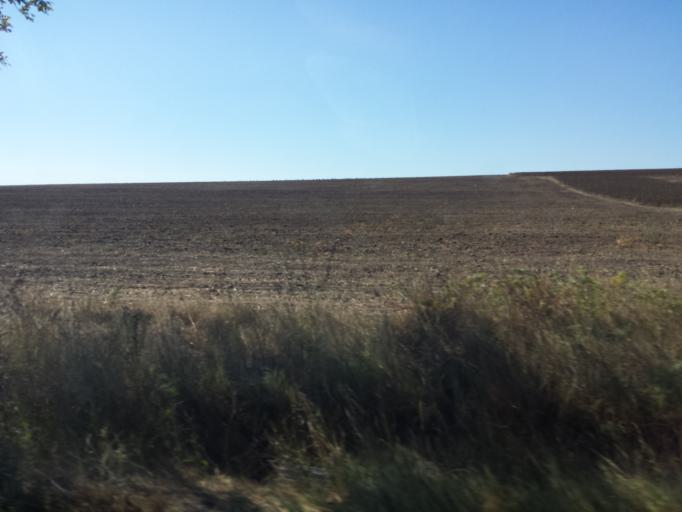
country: RO
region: Tulcea
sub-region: Comuna Frecatei
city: Cataloi
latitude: 45.1278
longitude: 28.7542
